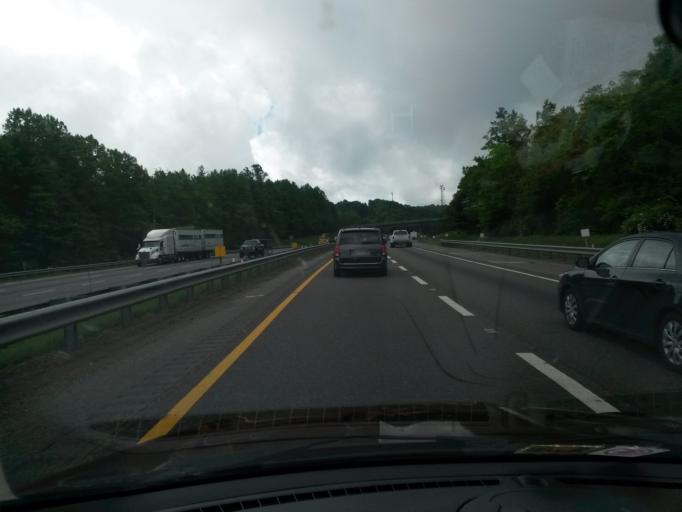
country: US
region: Virginia
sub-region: Carroll County
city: Cana
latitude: 36.6549
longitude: -80.7054
